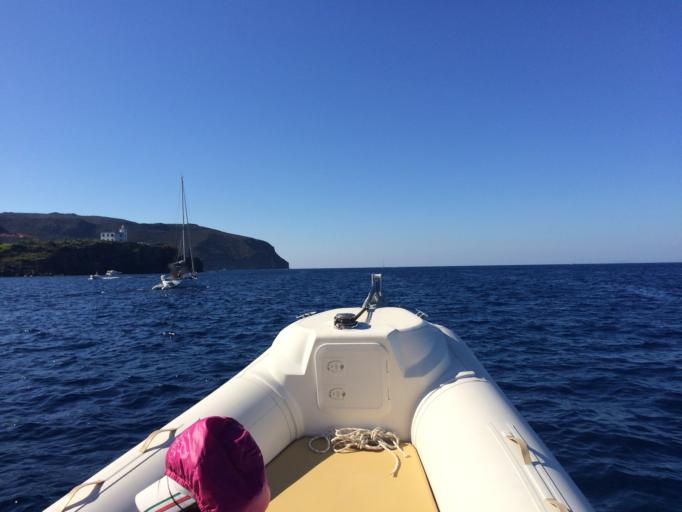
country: IT
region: Tuscany
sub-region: Provincia di Livorno
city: Capraia Isola
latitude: 43.0480
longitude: 9.8480
